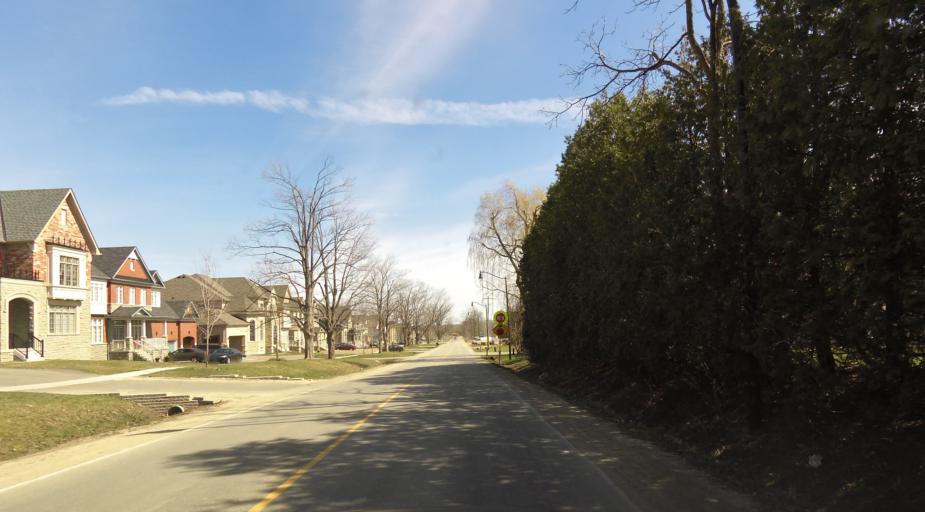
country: CA
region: Ontario
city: Brampton
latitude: 43.6523
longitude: -79.7862
